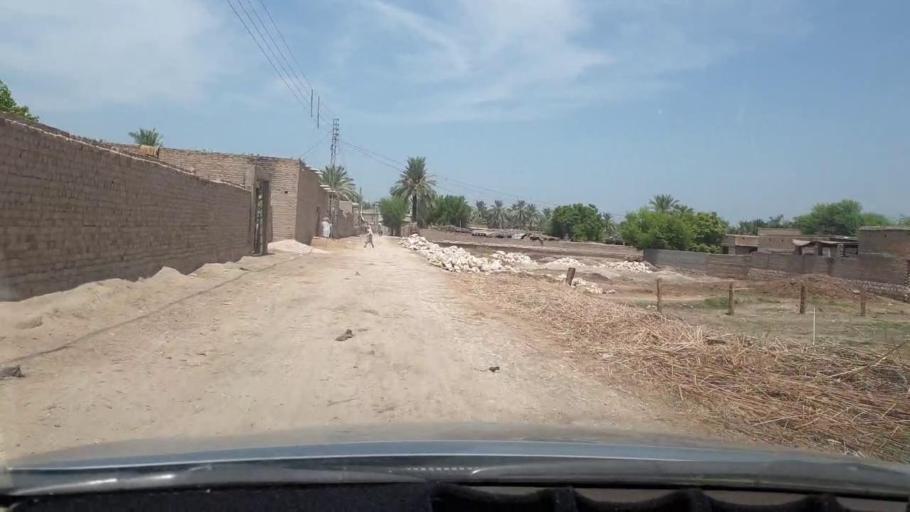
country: PK
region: Sindh
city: Khairpur
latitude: 27.4751
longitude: 68.7644
